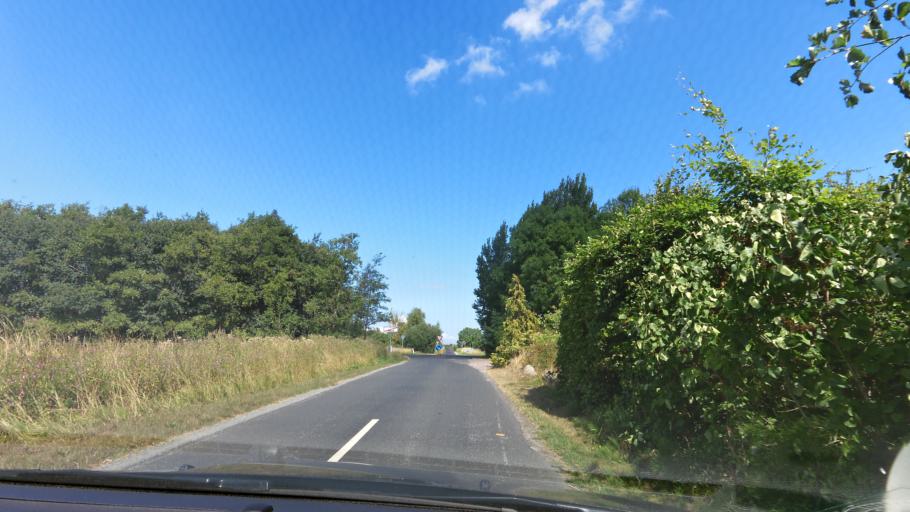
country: DK
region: South Denmark
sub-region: Nordfyns Kommune
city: Otterup
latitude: 55.5521
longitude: 10.4757
